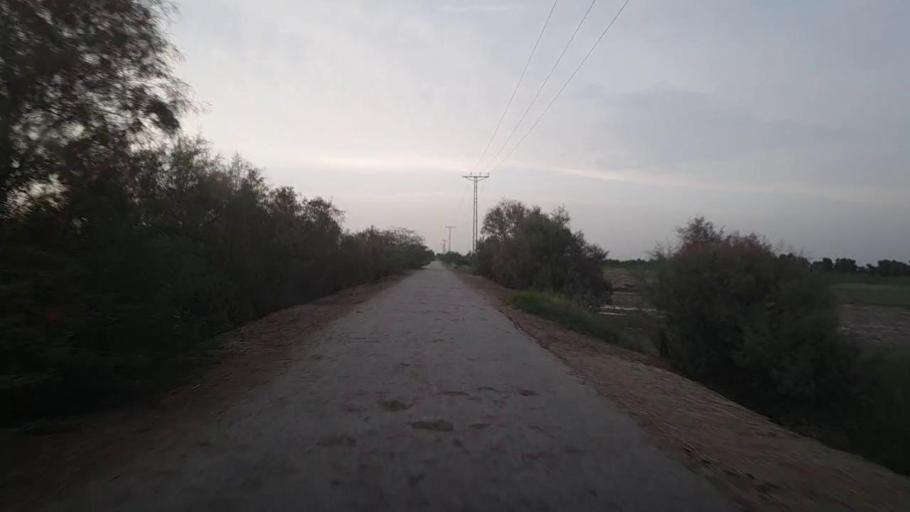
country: PK
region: Sindh
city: Karaundi
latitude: 27.0070
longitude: 68.3539
